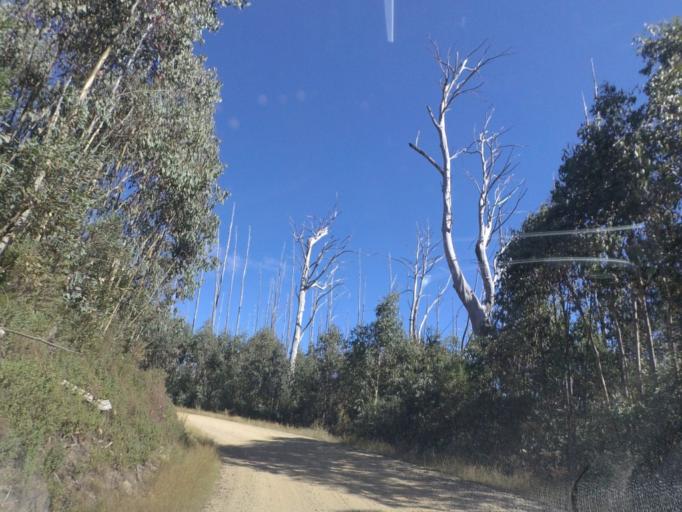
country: AU
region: Victoria
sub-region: Murrindindi
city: Alexandra
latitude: -37.4314
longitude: 145.8028
